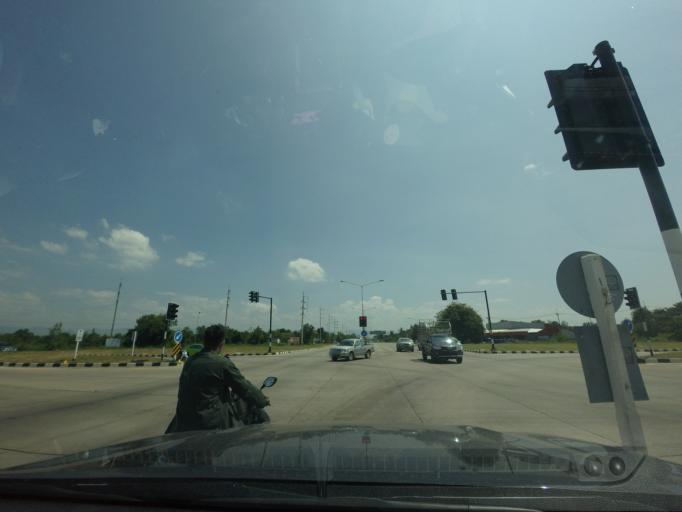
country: TH
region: Phetchabun
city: Lom Sak
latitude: 16.7653
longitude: 101.1854
